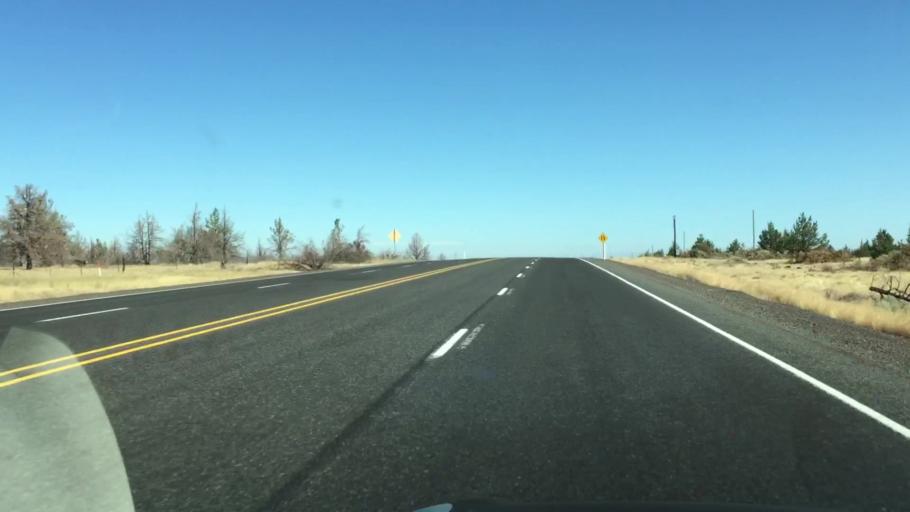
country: US
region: Oregon
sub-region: Jefferson County
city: Madras
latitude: 44.9028
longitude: -120.9380
